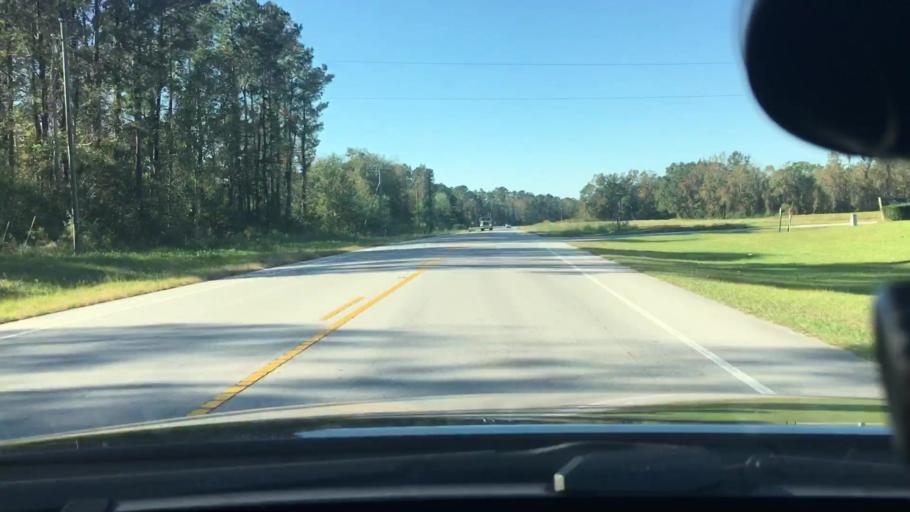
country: US
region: North Carolina
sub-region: Craven County
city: Trent Woods
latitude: 35.1706
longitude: -77.1270
